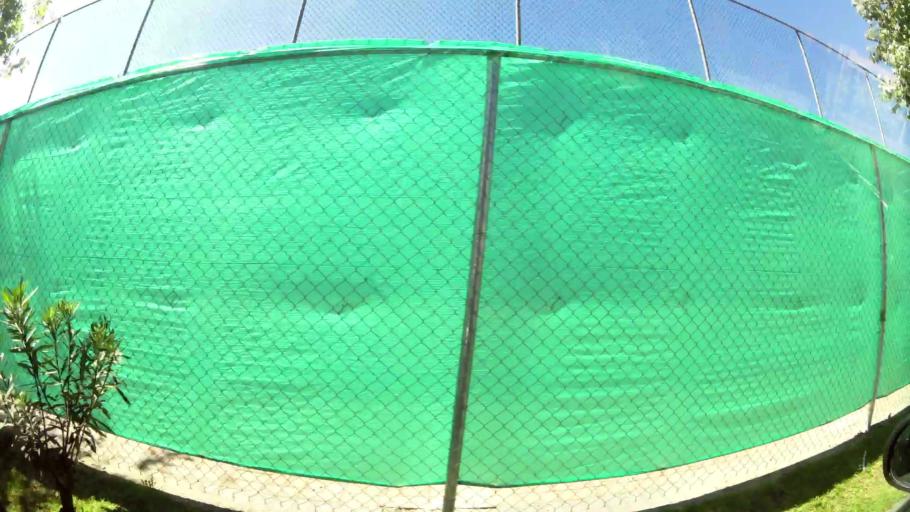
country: EC
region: Pichincha
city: Quito
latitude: -0.2584
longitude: -78.5341
